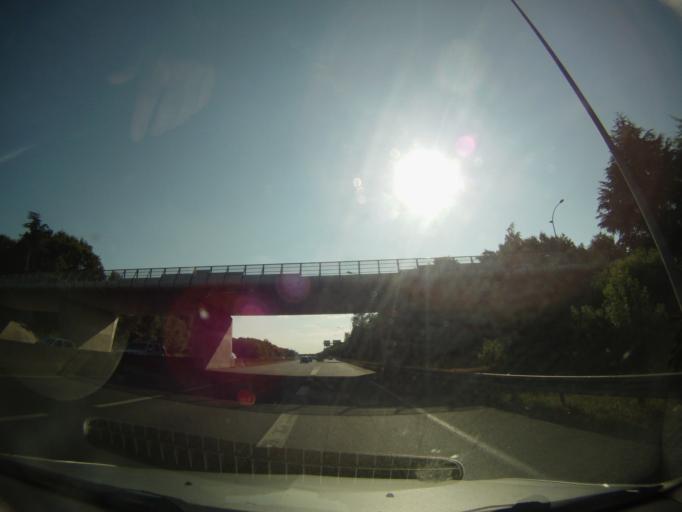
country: FR
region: Pays de la Loire
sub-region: Departement de la Loire-Atlantique
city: Orvault
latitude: 47.2672
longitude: -1.5818
